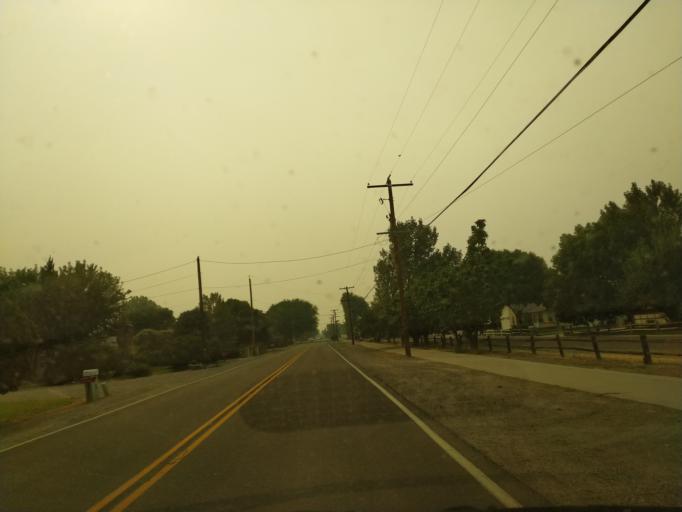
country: US
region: Colorado
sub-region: Mesa County
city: Fruitvale
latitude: 39.0847
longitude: -108.4848
